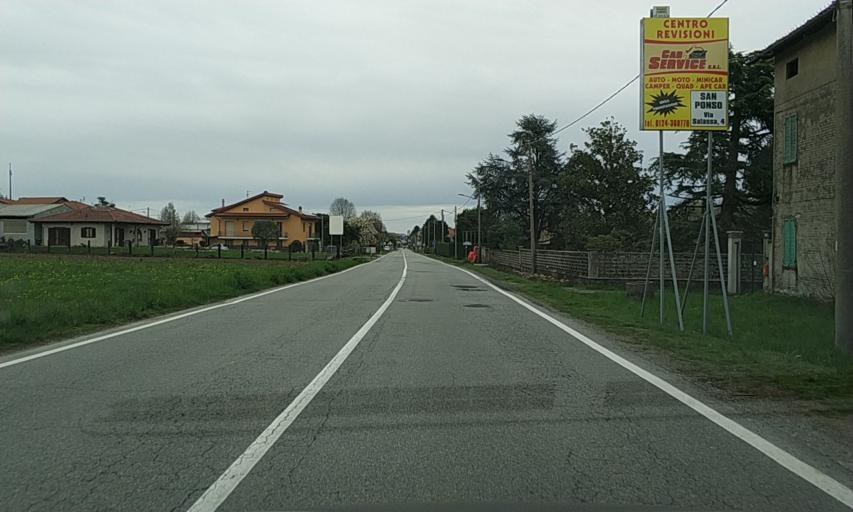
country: IT
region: Piedmont
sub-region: Provincia di Torino
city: Rivarolo Canavese
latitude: 45.3313
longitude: 7.7065
